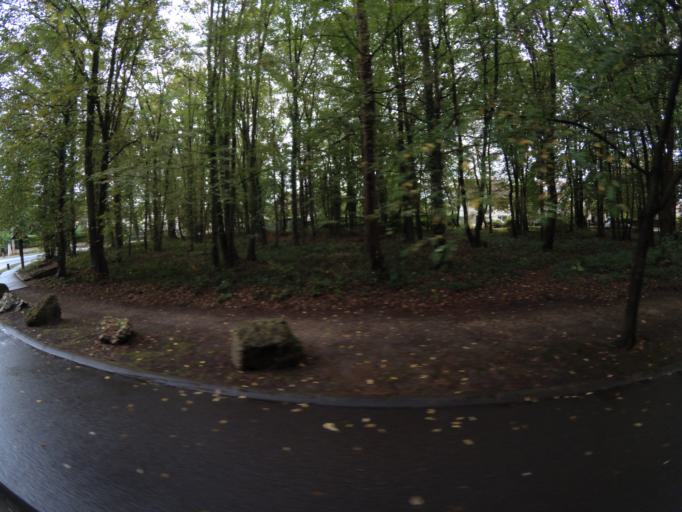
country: FR
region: Ile-de-France
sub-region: Departement de Seine-et-Marne
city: Chanteloup-en-Brie
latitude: 48.8602
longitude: 2.7352
